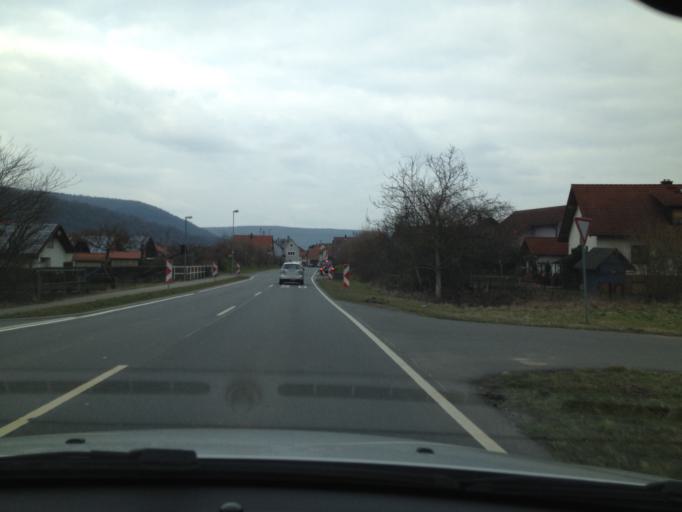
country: DE
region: Bavaria
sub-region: Regierungsbezirk Unterfranken
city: Stadtprozelten
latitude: 49.7802
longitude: 9.4128
